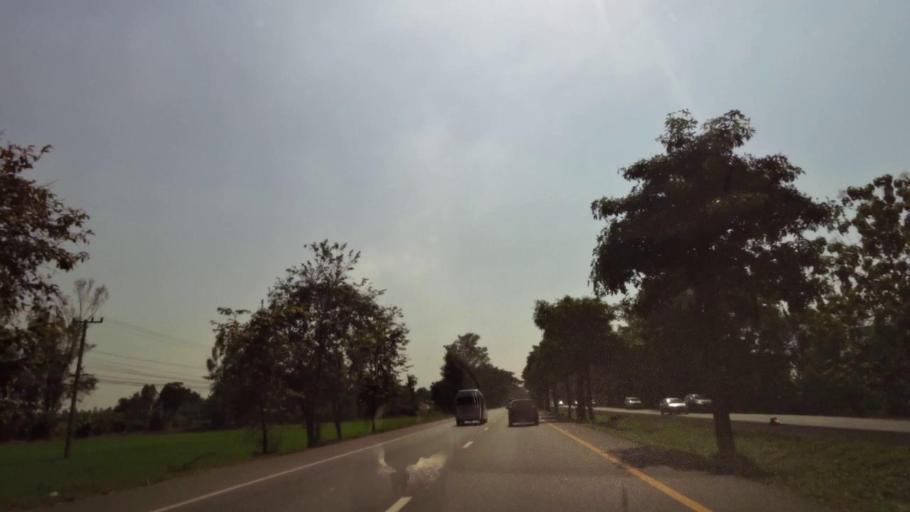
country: TH
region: Phichit
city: Bueng Na Rang
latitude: 16.0660
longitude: 100.1236
